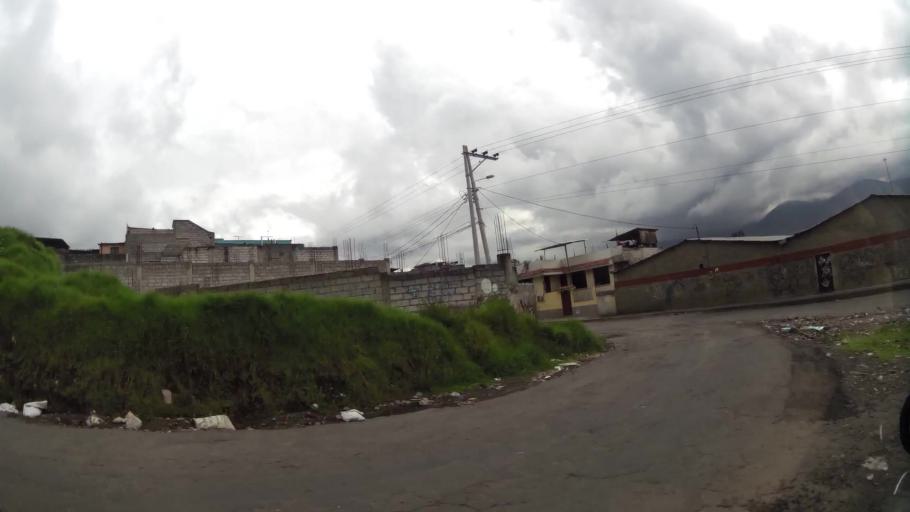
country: EC
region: Pichincha
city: Sangolqui
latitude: -0.3160
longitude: -78.5345
